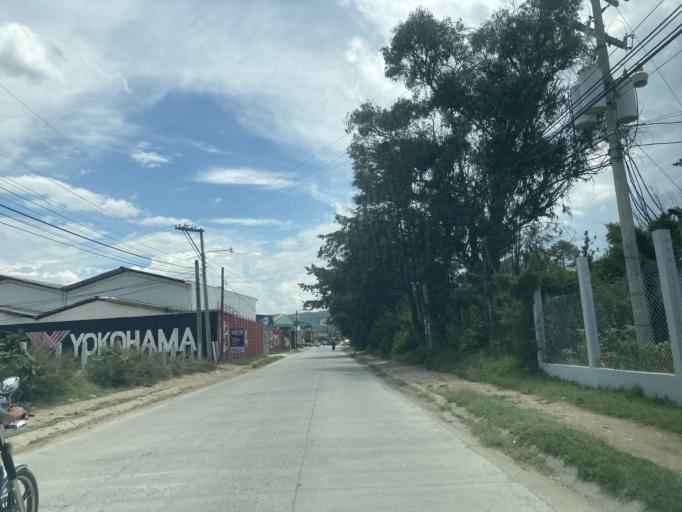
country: GT
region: Huehuetenango
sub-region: Municipio de Huehuetenango
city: Huehuetenango
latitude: 15.3112
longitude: -91.4937
